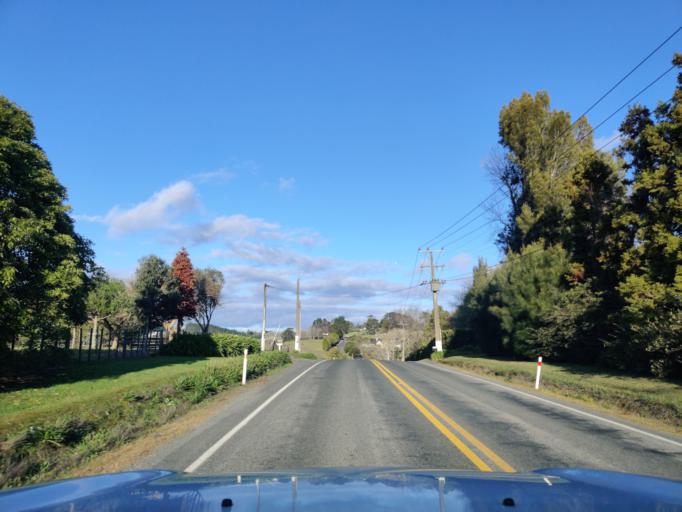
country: NZ
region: Auckland
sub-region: Auckland
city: Red Hill
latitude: -36.9620
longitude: 174.9774
